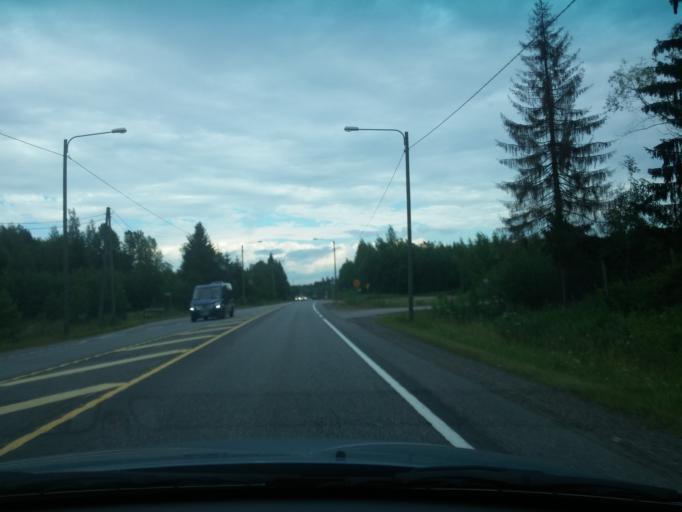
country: FI
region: Haeme
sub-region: Riihimaeki
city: Loppi
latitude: 60.7255
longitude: 24.5124
